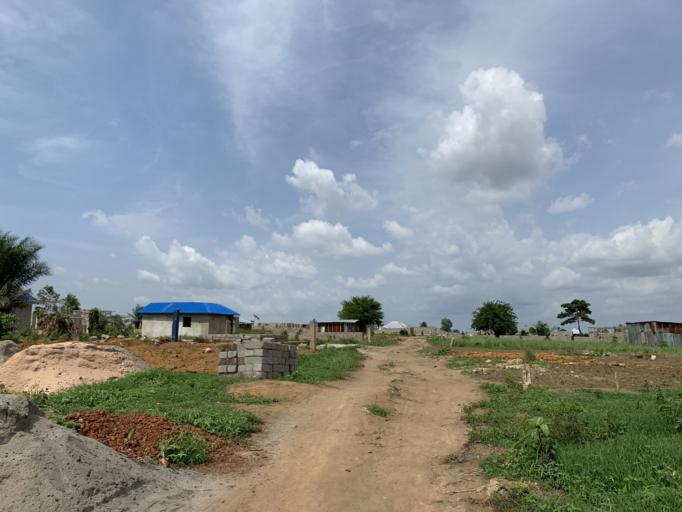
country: SL
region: Western Area
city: Waterloo
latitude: 8.3532
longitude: -13.0472
